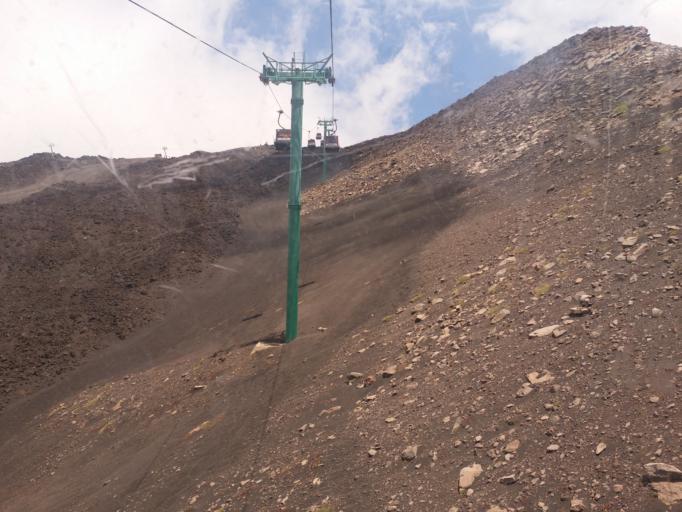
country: IT
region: Sicily
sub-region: Catania
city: Ragalna
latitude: 37.7141
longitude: 14.9998
